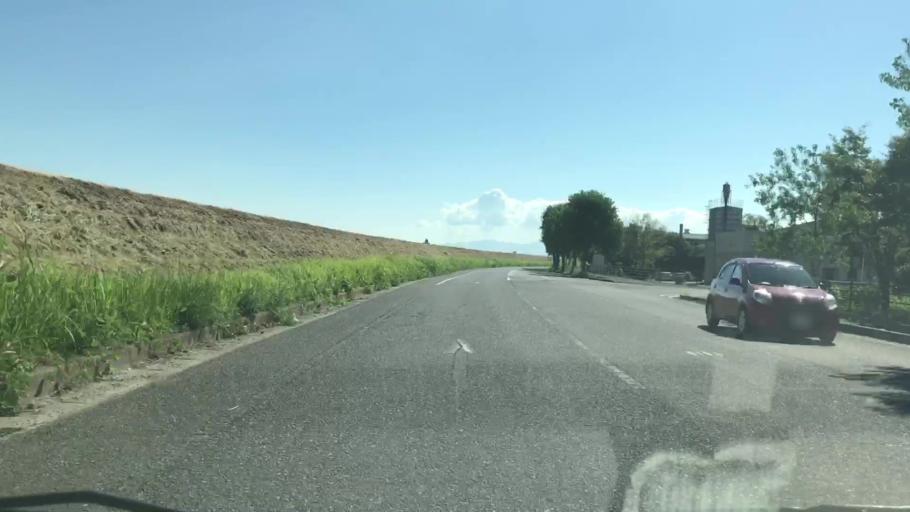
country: JP
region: Saga Prefecture
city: Okawa
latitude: 33.2304
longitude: 130.3765
